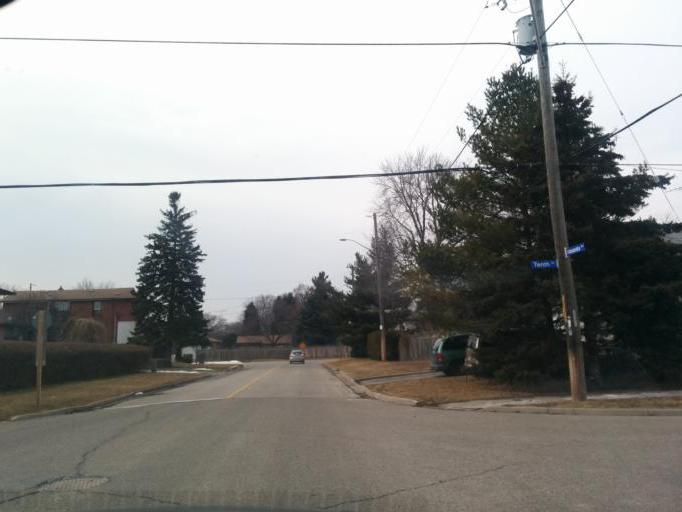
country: CA
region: Ontario
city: Etobicoke
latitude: 43.5841
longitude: -79.5741
